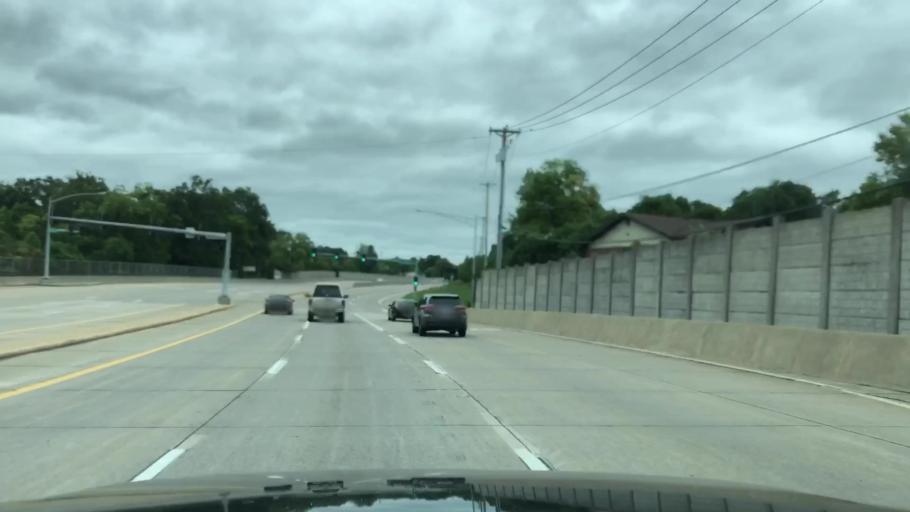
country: US
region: Missouri
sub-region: Saint Louis County
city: Manchester
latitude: 38.6094
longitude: -90.5113
